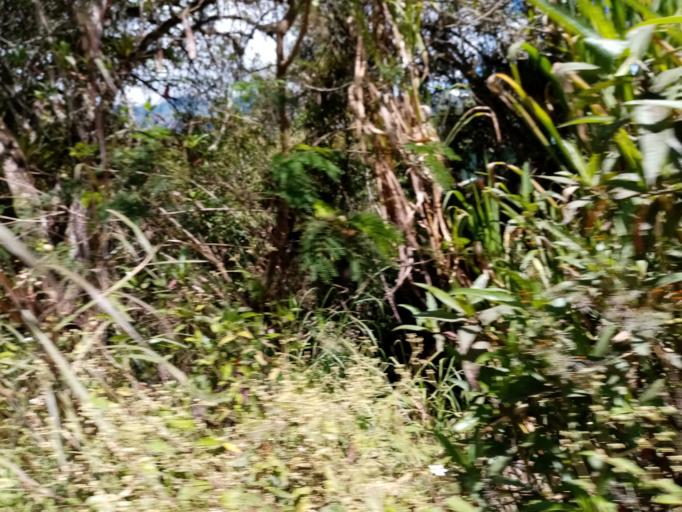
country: CO
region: Cundinamarca
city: Tenza
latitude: 5.0772
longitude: -73.4373
